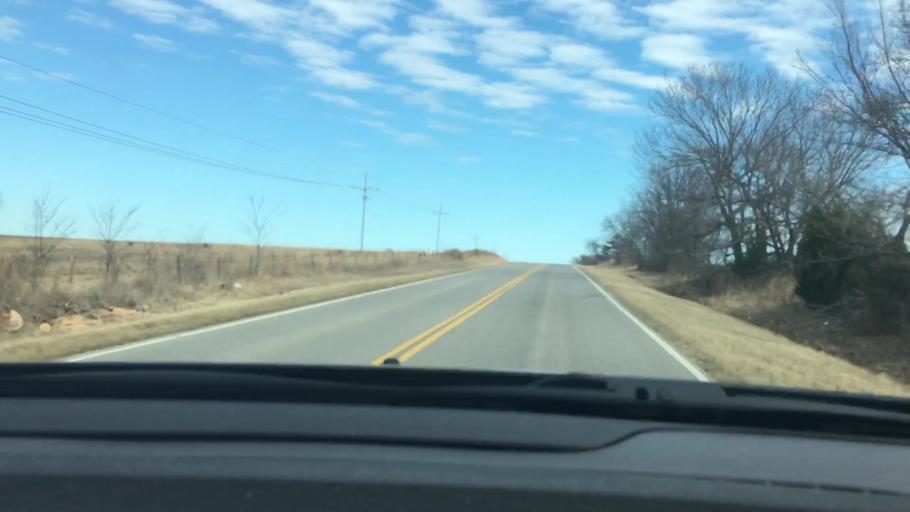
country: US
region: Oklahoma
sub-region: Garvin County
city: Stratford
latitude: 34.7967
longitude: -96.8359
